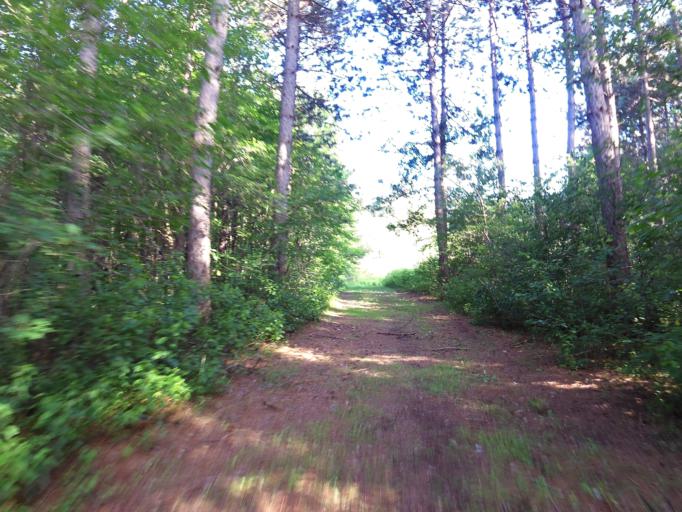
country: CA
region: Ontario
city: Bells Corners
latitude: 45.3180
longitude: -75.7391
